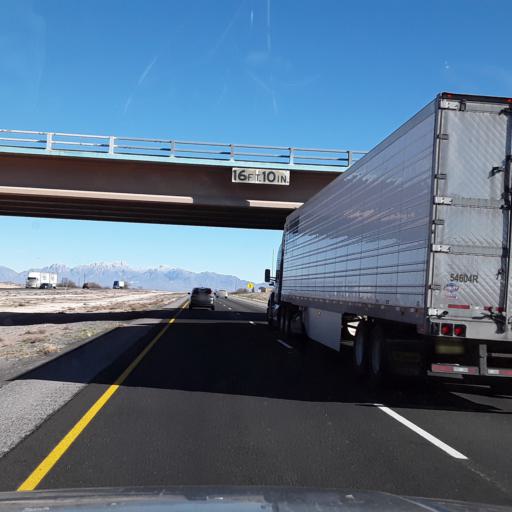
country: US
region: New Mexico
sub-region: Dona Ana County
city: Mesilla
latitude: 32.2719
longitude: -106.9222
